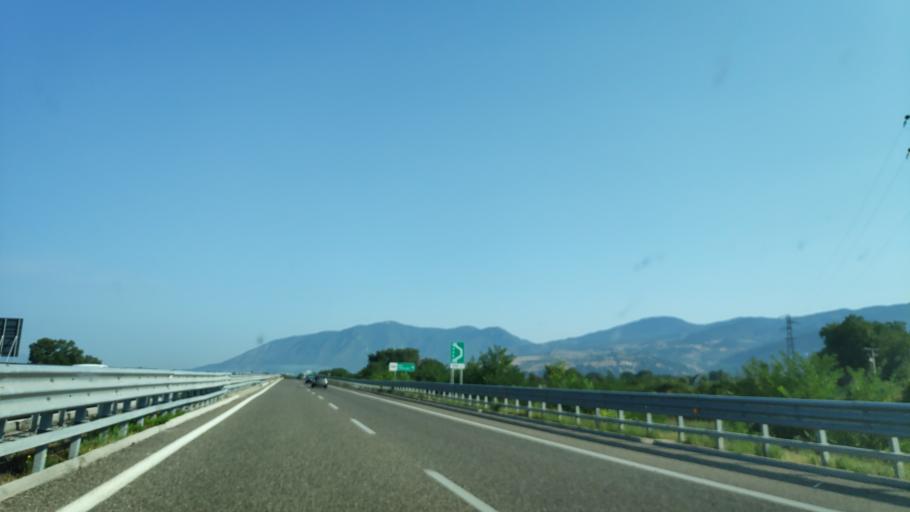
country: IT
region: Campania
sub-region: Provincia di Salerno
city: Padula
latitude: 40.3186
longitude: 15.6394
